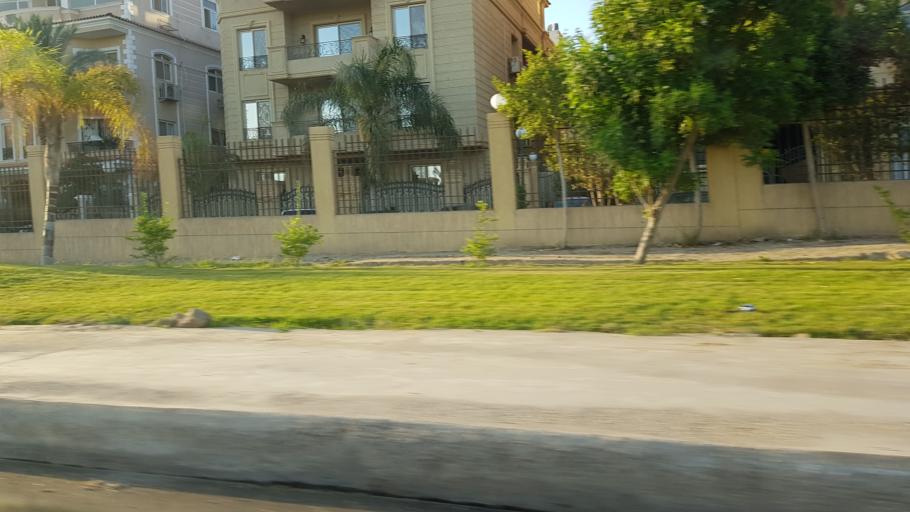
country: EG
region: Muhafazat al Qalyubiyah
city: Al Khankah
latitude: 30.0623
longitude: 31.4376
